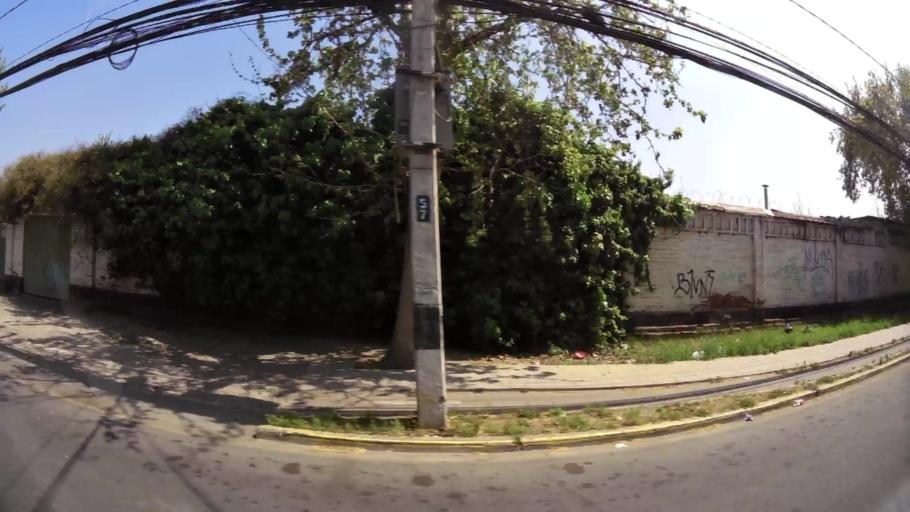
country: CL
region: Santiago Metropolitan
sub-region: Provincia de Santiago
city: Santiago
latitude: -33.4688
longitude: -70.6650
